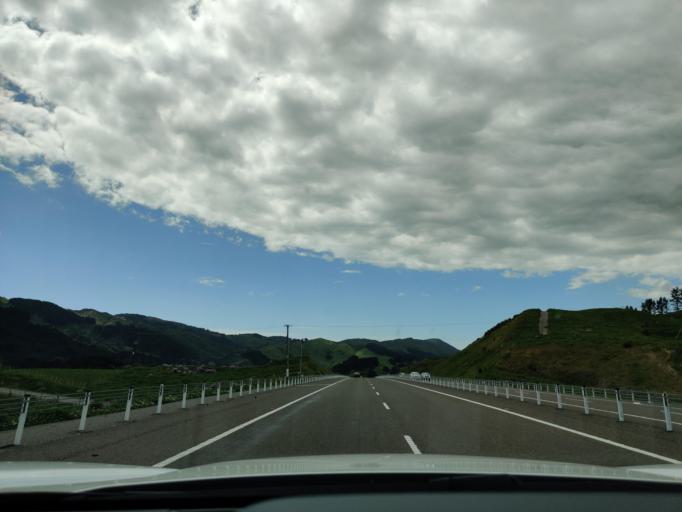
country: NZ
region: Wellington
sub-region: Porirua City
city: Porirua
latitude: -41.0766
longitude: 174.9420
